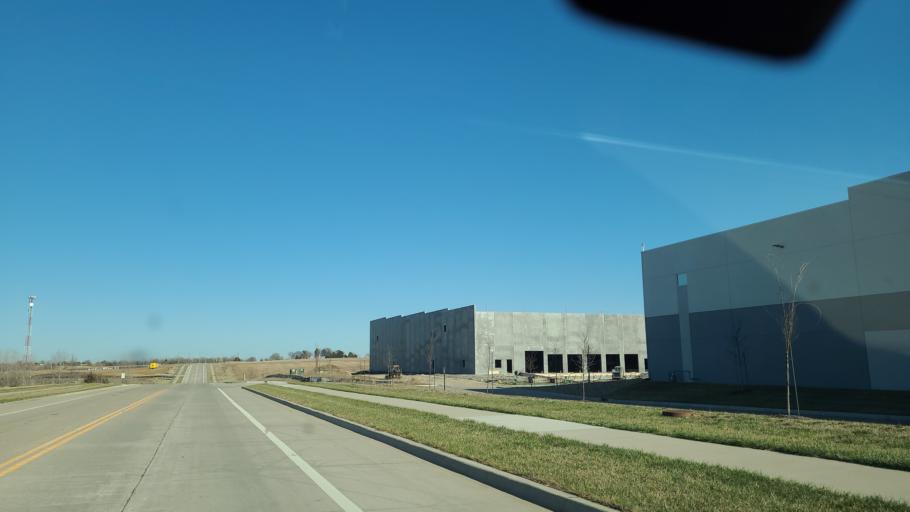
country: US
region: Kansas
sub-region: Douglas County
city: Lawrence
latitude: 38.9450
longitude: -95.2034
